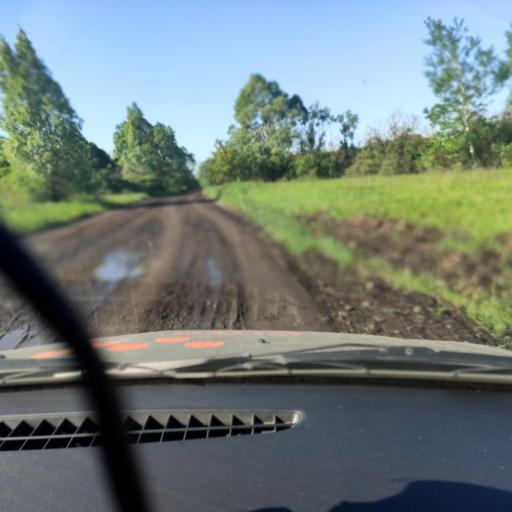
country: RU
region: Bashkortostan
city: Avdon
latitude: 54.5625
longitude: 55.8278
